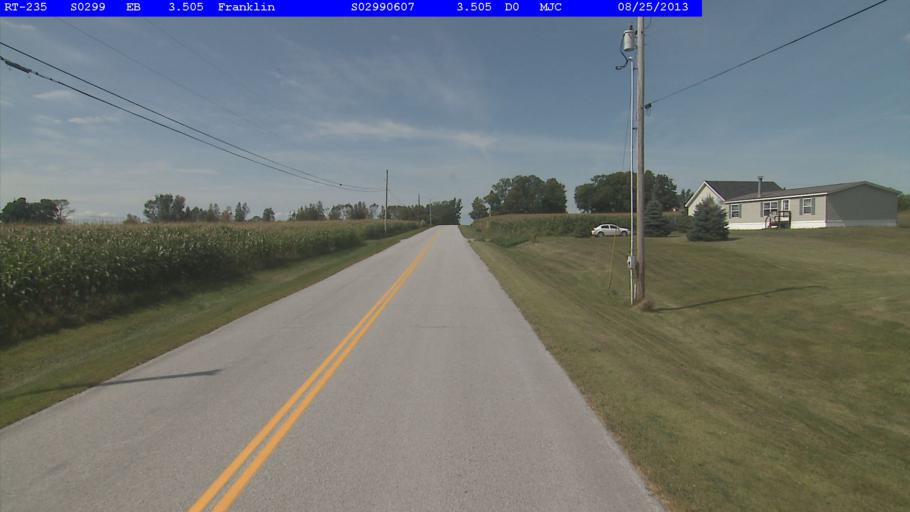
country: CA
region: Quebec
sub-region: Monteregie
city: Bedford
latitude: 45.0036
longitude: -72.9697
